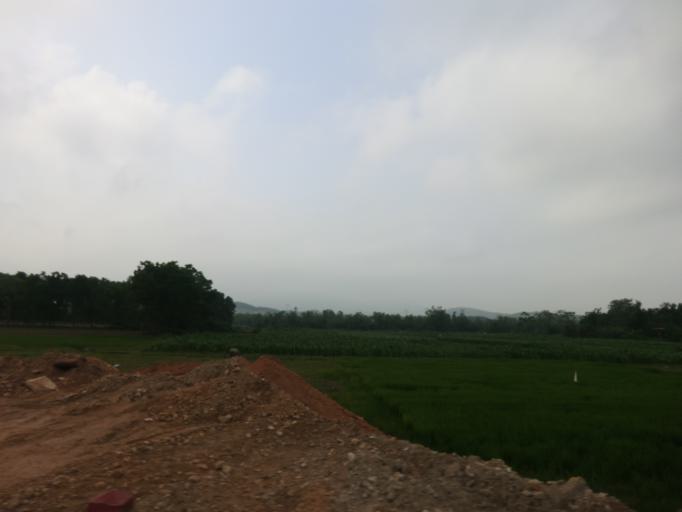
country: VN
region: Quang Binh
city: Hoan Lao
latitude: 17.6224
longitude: 106.4134
